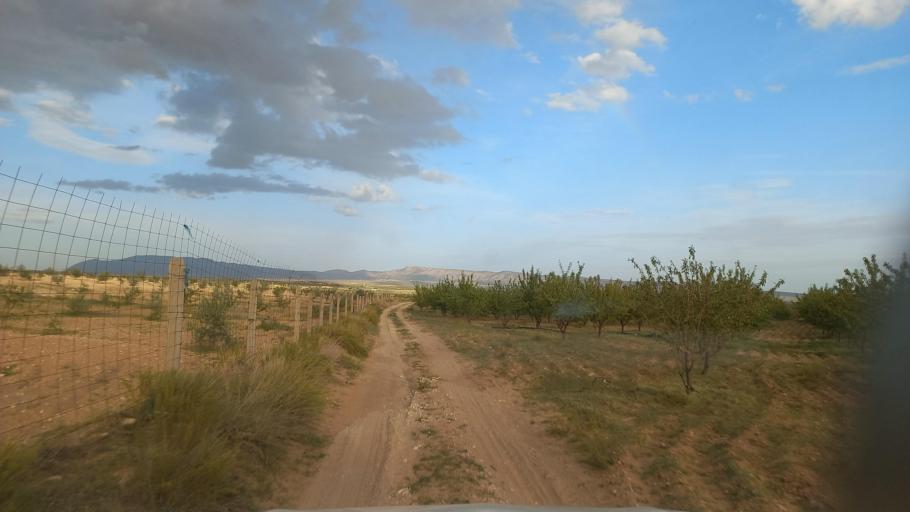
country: TN
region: Al Qasrayn
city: Sbiba
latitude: 35.3515
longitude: 9.0172
